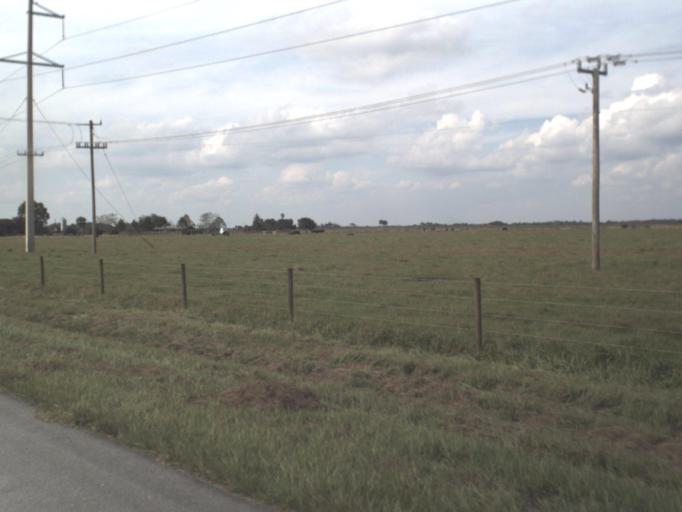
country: US
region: Florida
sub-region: Okeechobee County
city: Taylor Creek
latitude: 27.1934
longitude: -80.7291
